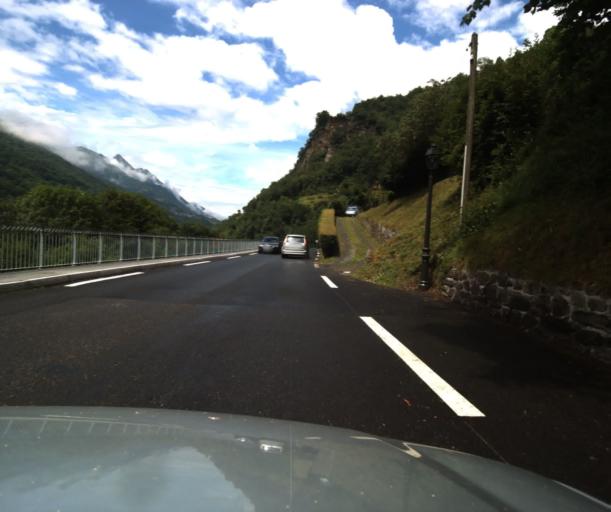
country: FR
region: Midi-Pyrenees
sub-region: Departement des Hautes-Pyrenees
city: Luz-Saint-Sauveur
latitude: 42.8606
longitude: -0.0057
